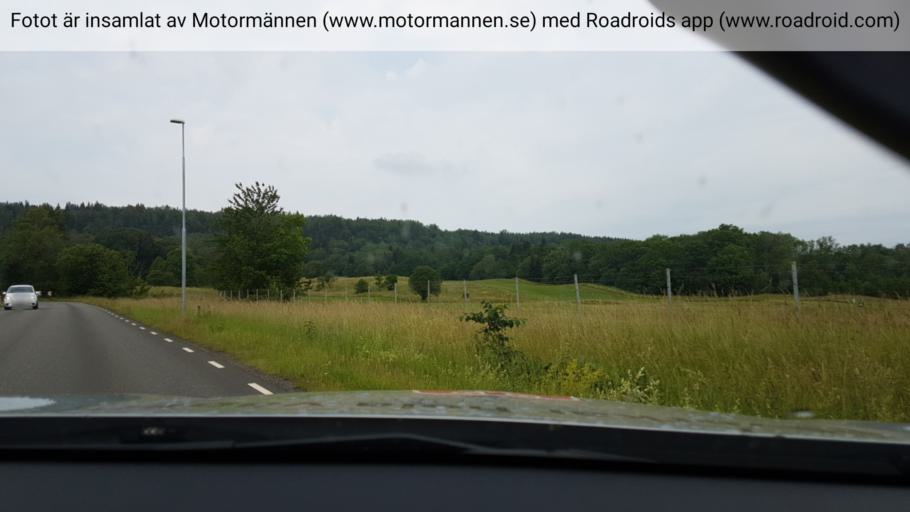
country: SE
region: Vaestra Goetaland
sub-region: Skovde Kommun
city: Skultorp
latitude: 58.3738
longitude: 13.8154
